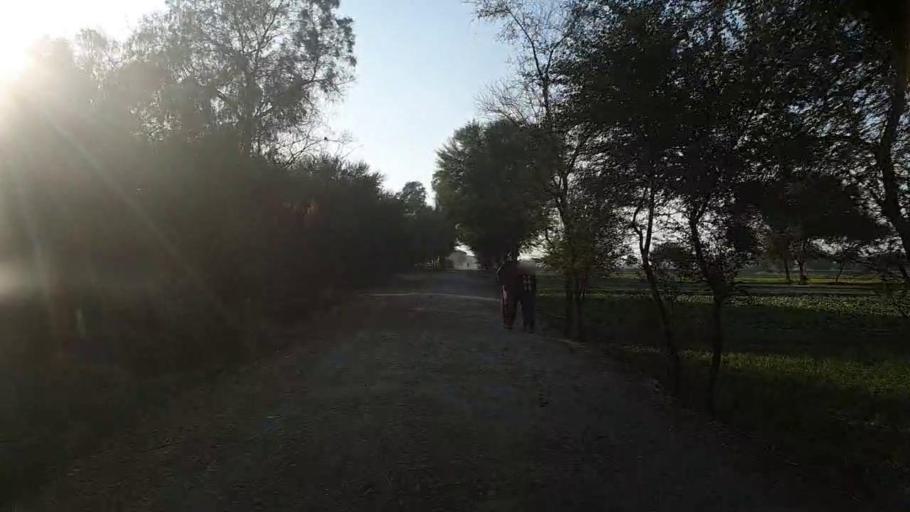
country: PK
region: Sindh
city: Pad Idan
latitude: 26.7341
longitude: 68.3292
